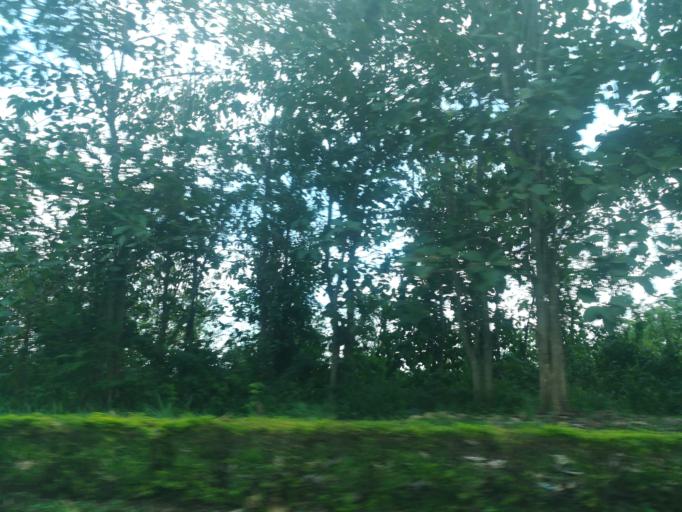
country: NG
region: Lagos
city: Ikorodu
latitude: 6.6410
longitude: 3.5219
